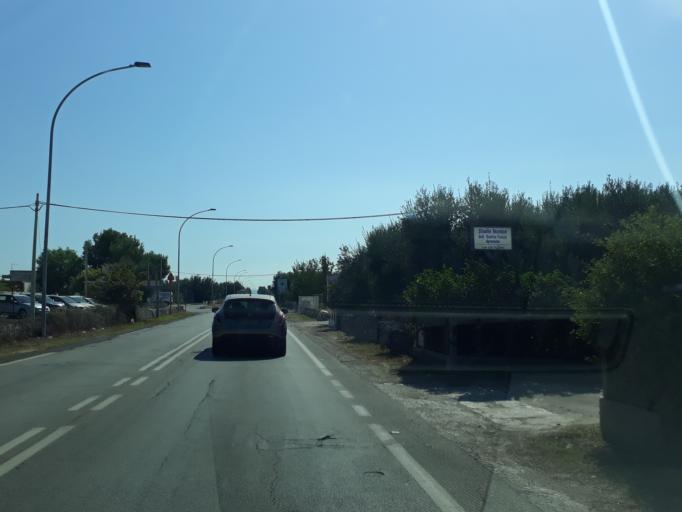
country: IT
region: Apulia
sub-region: Provincia di Bari
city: Monopoli
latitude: 40.9372
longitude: 17.3085
